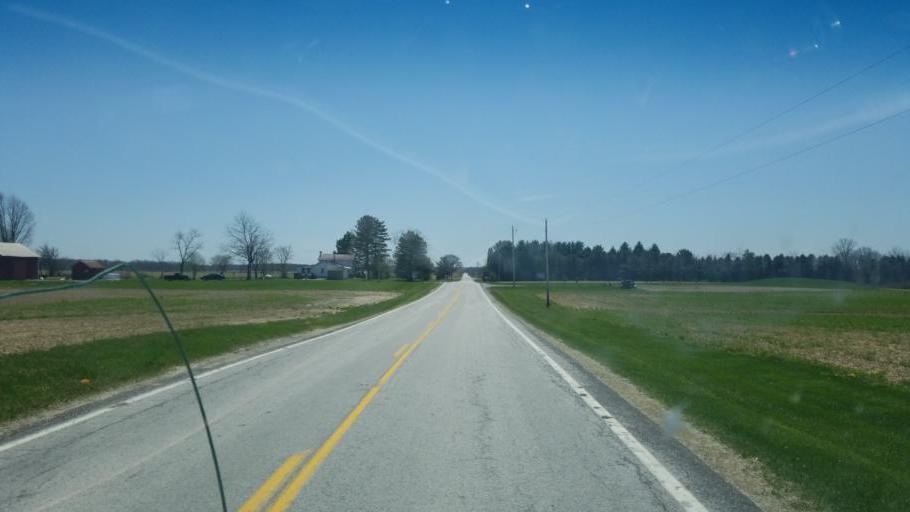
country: US
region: Ohio
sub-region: Huron County
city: New London
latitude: 41.0944
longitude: -82.3478
